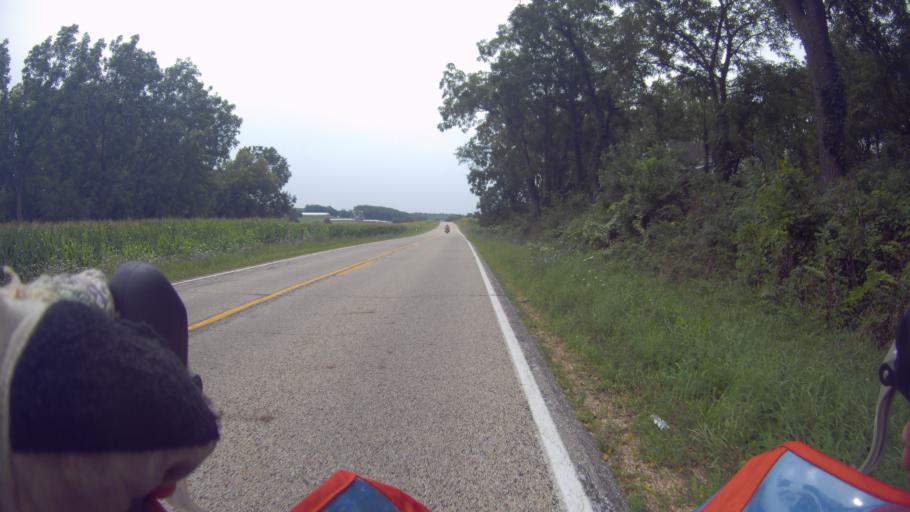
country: US
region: Wisconsin
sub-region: Dane County
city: Mount Horeb
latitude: 42.9160
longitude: -89.6956
